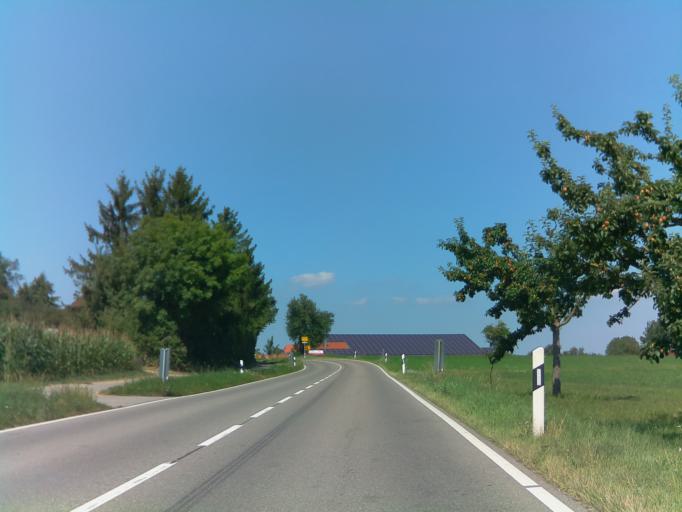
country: DE
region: Baden-Wuerttemberg
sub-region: Regierungsbezirk Stuttgart
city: Eberdingen
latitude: 48.8451
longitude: 8.9791
